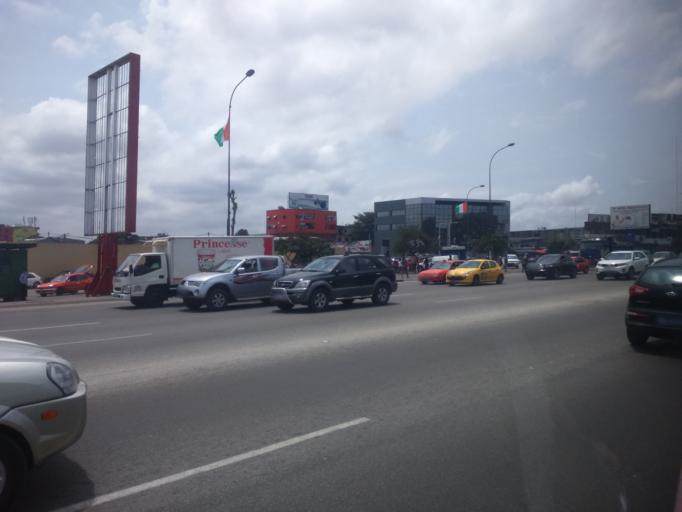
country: CI
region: Lagunes
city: Abidjan
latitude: 5.3006
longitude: -3.9898
